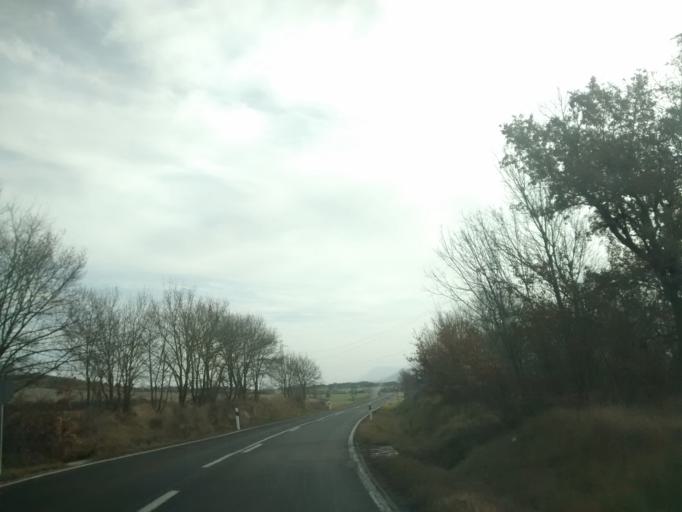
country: ES
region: Aragon
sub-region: Provincia de Zaragoza
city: Siguees
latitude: 42.6159
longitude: -1.0625
